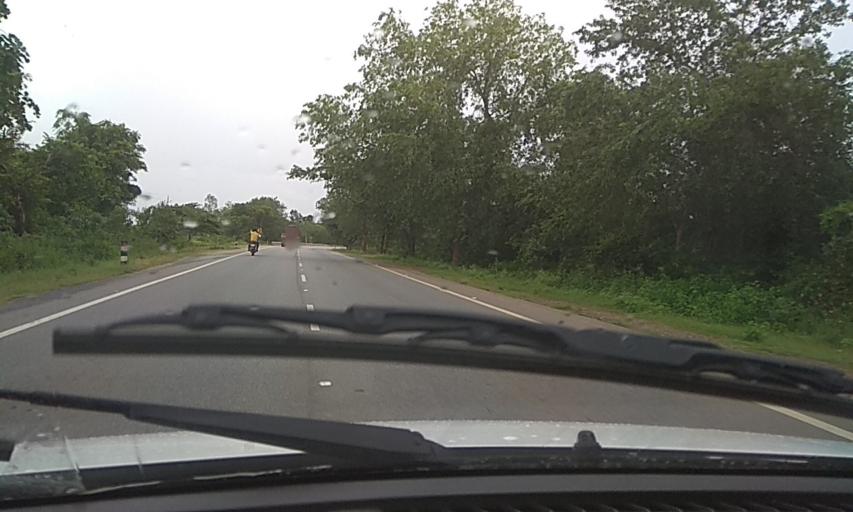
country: IN
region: Karnataka
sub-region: Mandya
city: Maddur
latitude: 12.7964
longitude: 77.0425
